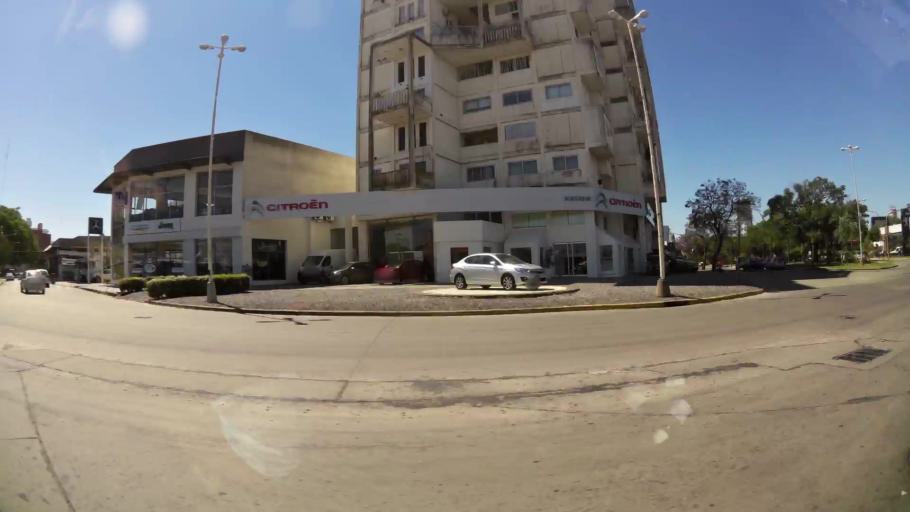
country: AR
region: Santa Fe
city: Santa Fe de la Vera Cruz
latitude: -31.6469
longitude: -60.7020
